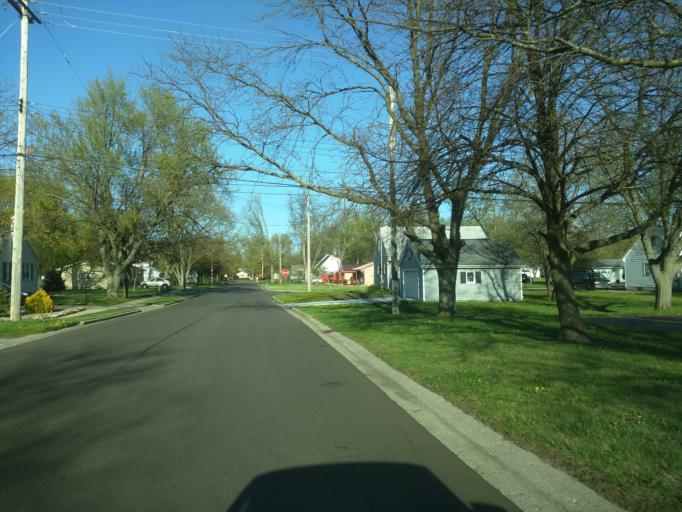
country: US
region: Michigan
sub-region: Eaton County
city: Waverly
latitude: 42.7374
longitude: -84.6205
